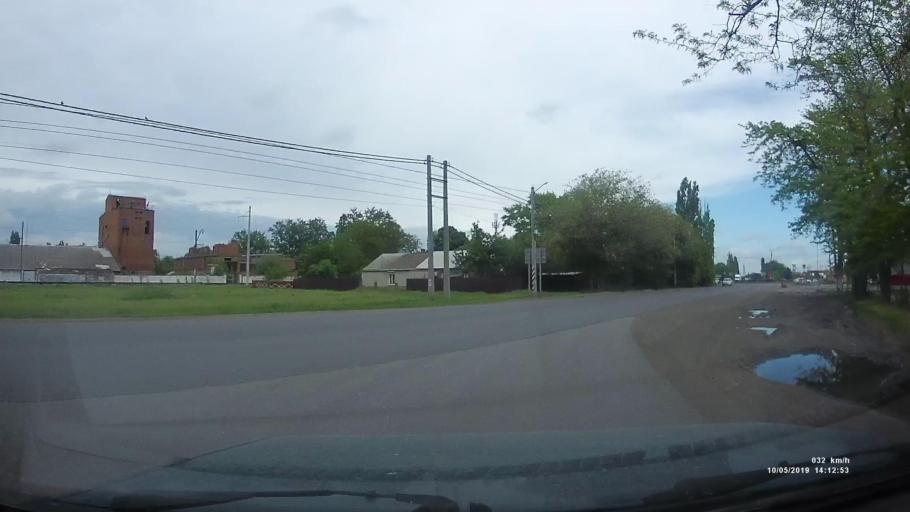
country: RU
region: Rostov
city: Azov
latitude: 47.0924
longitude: 39.4300
